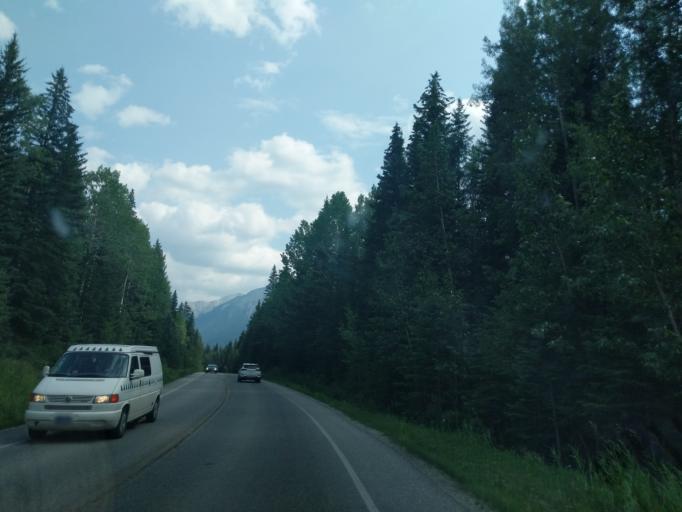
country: CA
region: Alberta
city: Banff
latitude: 51.1757
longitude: -115.7163
